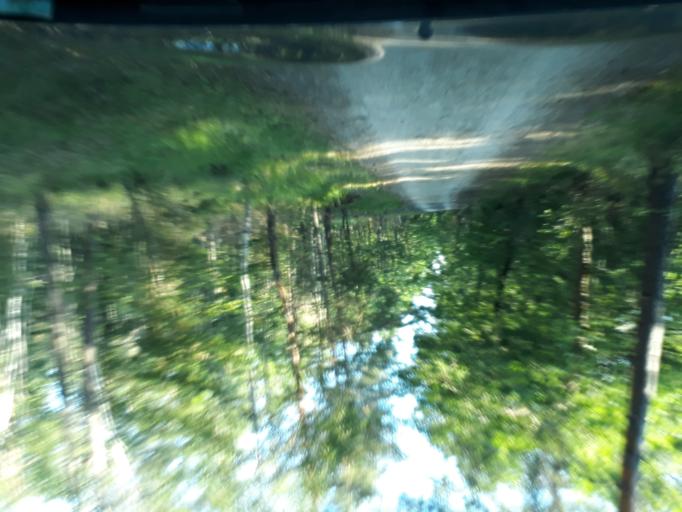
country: FR
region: Centre
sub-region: Departement du Loiret
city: Chaingy
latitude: 47.9084
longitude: 1.7417
